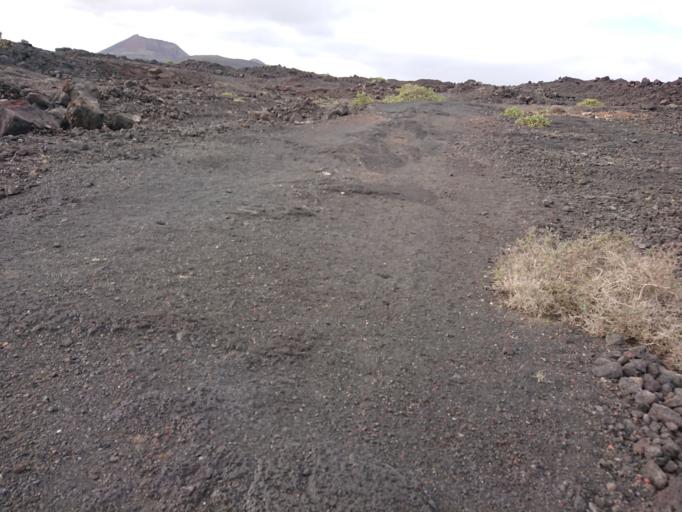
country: ES
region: Canary Islands
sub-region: Provincia de Las Palmas
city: Tias
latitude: 29.0013
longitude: -13.6913
